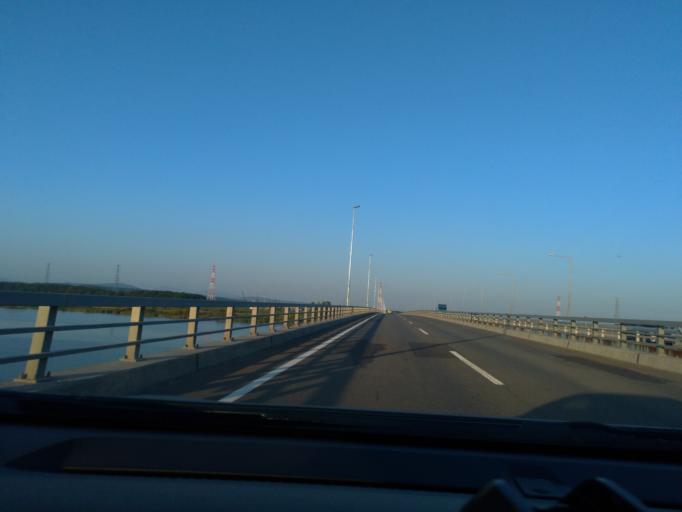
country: JP
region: Hokkaido
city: Ishikari
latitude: 43.1721
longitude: 141.4178
